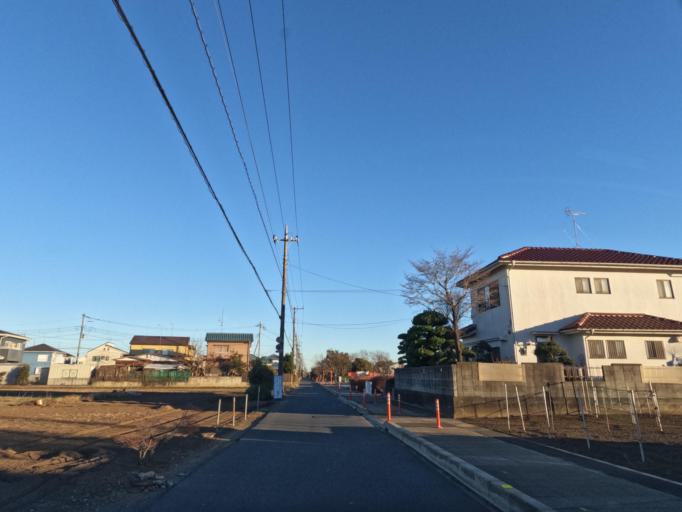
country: JP
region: Saitama
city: Iwatsuki
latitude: 35.9630
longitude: 139.6794
